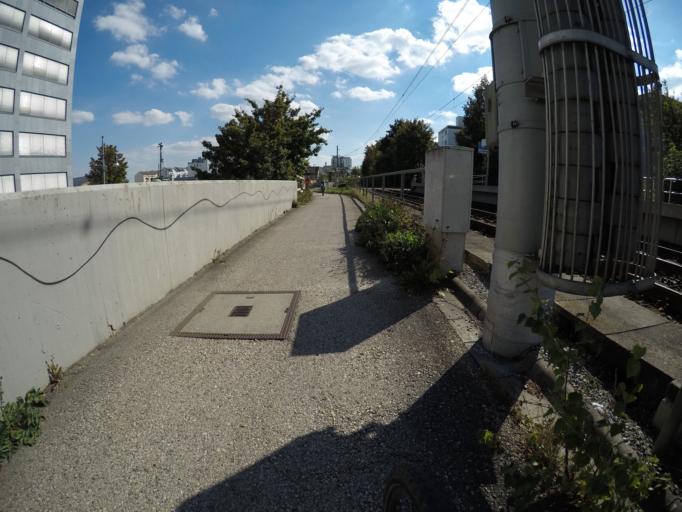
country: DE
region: Baden-Wuerttemberg
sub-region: Regierungsbezirk Stuttgart
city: Leinfelden-Echterdingen
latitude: 48.7076
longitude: 9.1429
